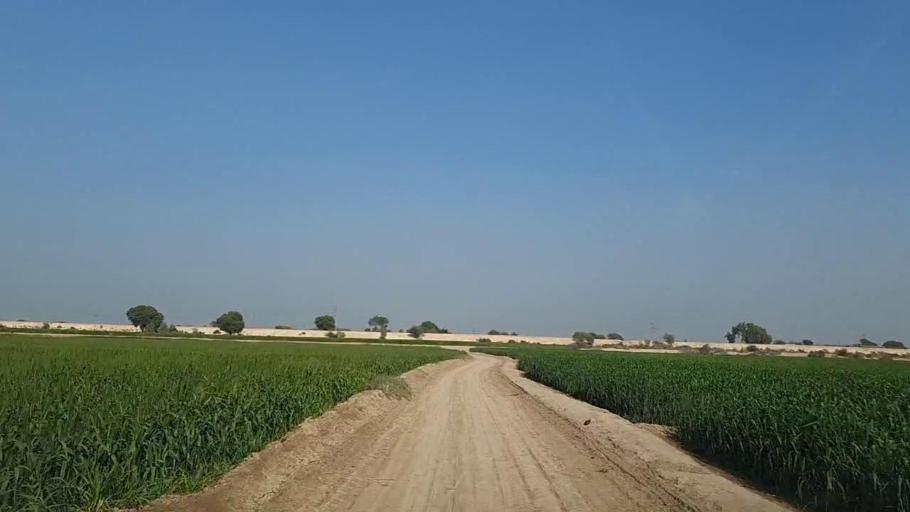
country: PK
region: Sindh
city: Moro
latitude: 26.6803
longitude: 67.9408
